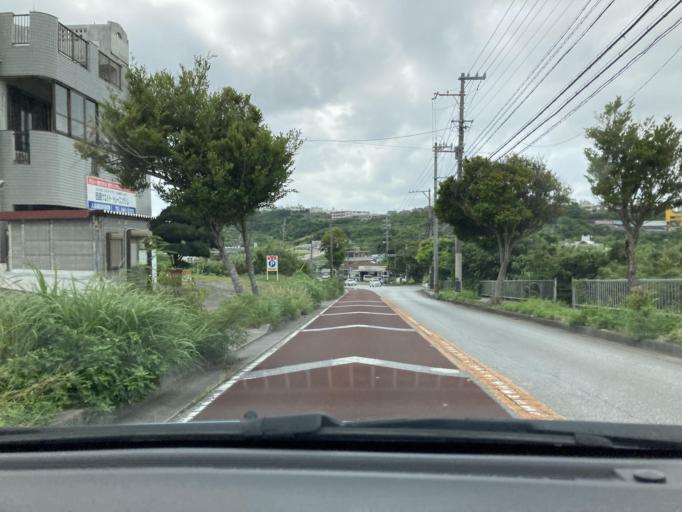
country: JP
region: Okinawa
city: Ginowan
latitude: 26.2347
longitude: 127.7431
